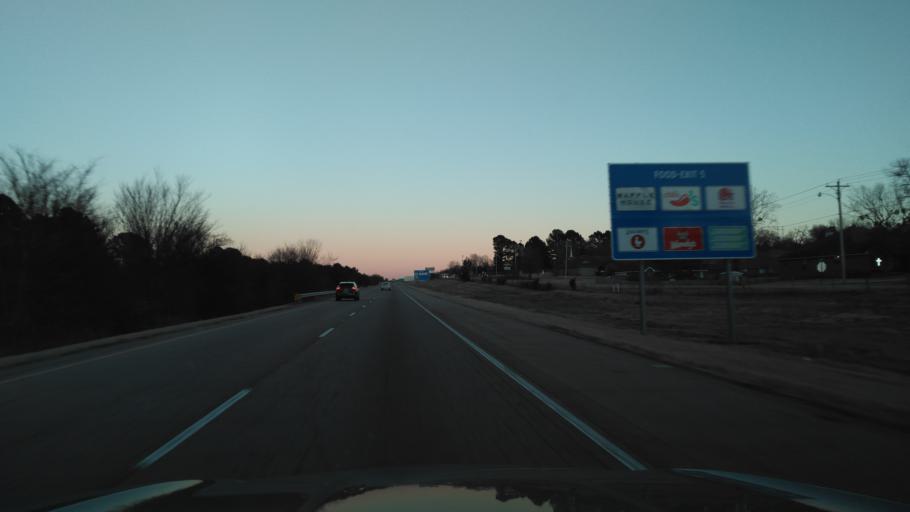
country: US
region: Arkansas
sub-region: Crawford County
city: Van Buren
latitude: 35.4651
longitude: -94.3748
